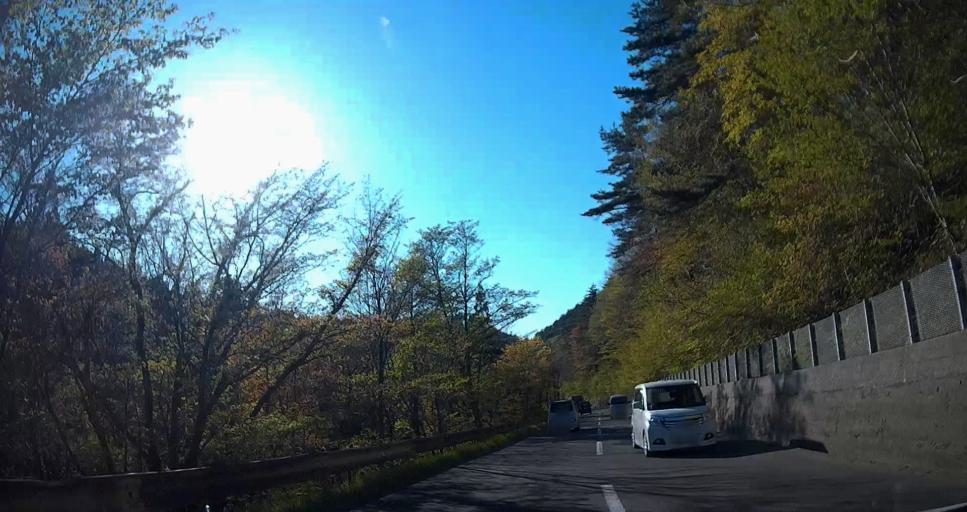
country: JP
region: Aomori
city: Mutsu
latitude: 41.4221
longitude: 141.1474
